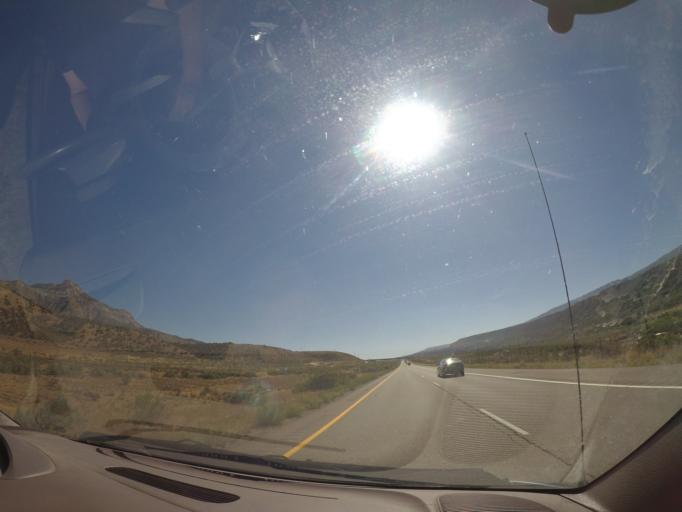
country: US
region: Colorado
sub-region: Garfield County
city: Battlement Mesa
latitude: 39.4758
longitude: -108.0027
